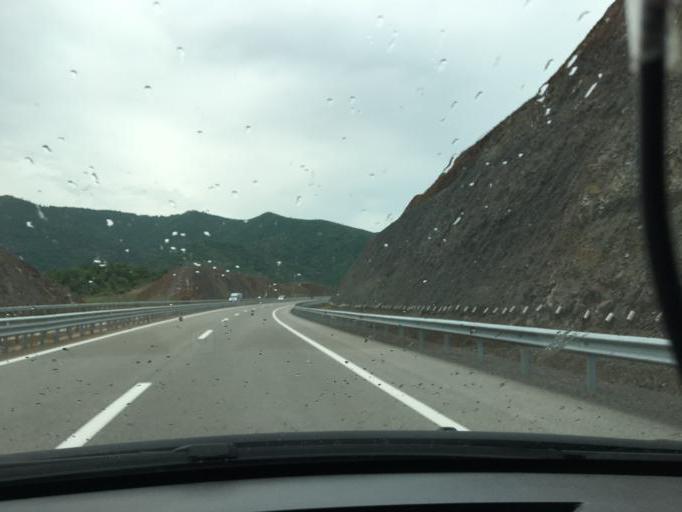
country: MK
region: Gevgelija
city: Miravci
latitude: 41.3522
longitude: 22.3634
